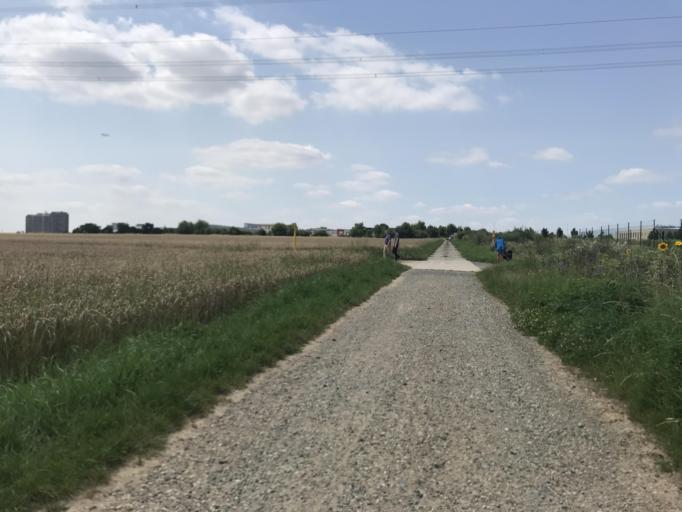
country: DE
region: Hesse
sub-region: Regierungsbezirk Darmstadt
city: Hochheim am Main
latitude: 50.0184
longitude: 8.3773
